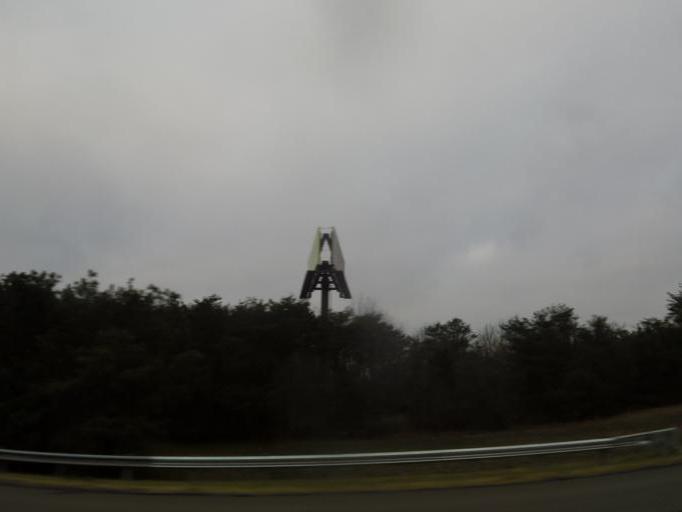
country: US
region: Alabama
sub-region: Jefferson County
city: Morris
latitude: 33.7252
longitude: -86.8256
